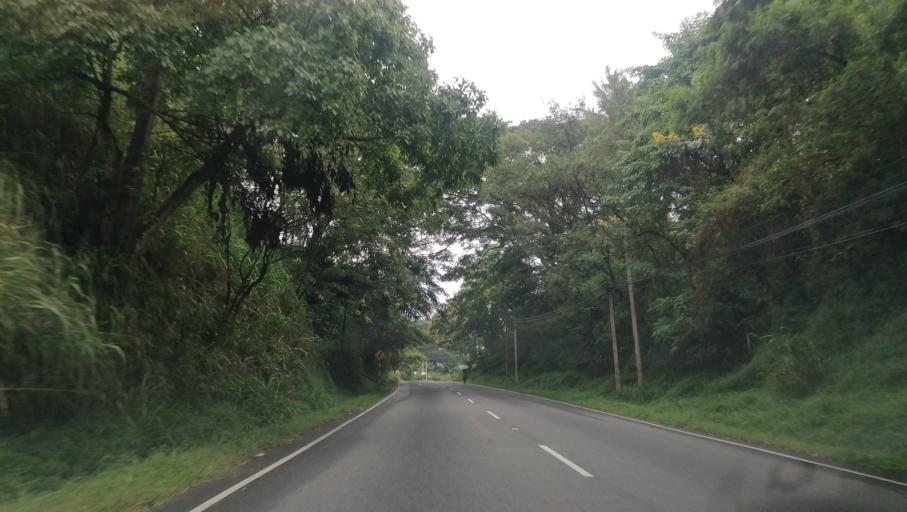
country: LK
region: Central
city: Kandy
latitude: 7.2511
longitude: 80.7314
